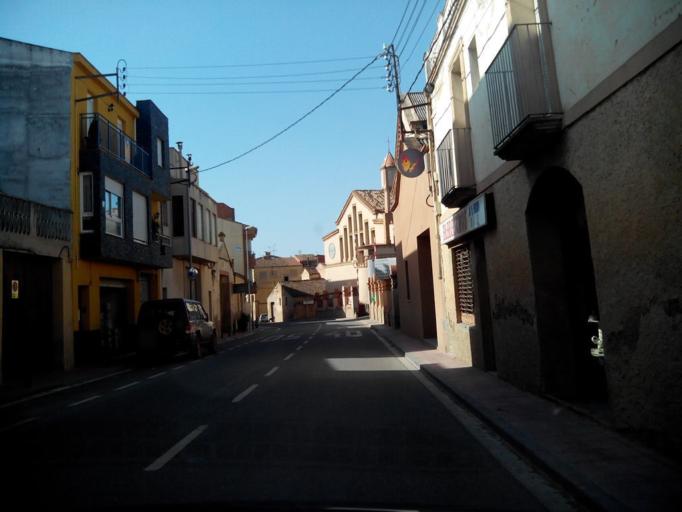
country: ES
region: Catalonia
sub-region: Provincia de Tarragona
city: Fores
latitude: 41.4464
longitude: 1.2474
